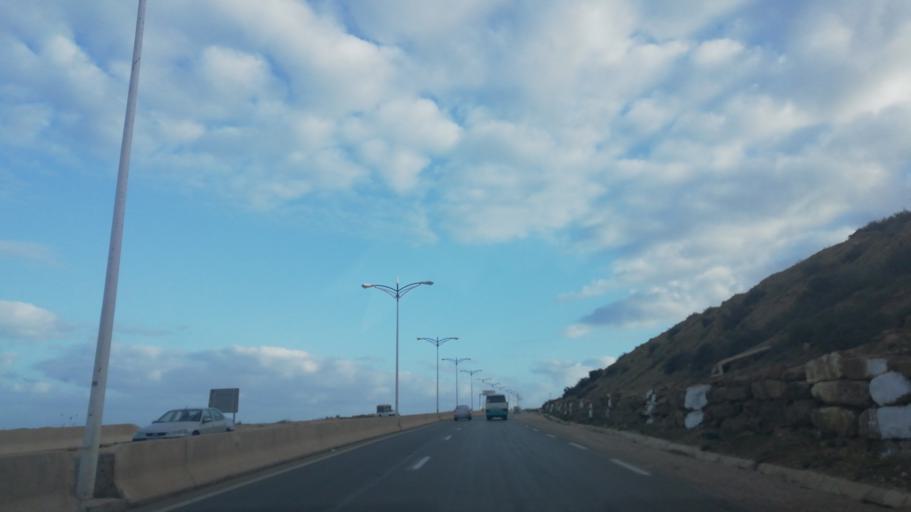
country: DZ
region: Mostaganem
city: Mostaganem
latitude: 36.0376
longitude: 0.1432
